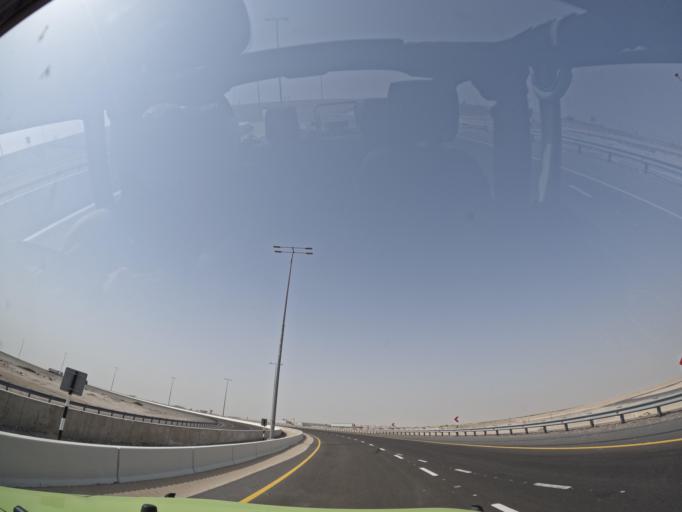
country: AE
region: Dubai
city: Dubai
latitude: 24.7912
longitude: 55.0757
